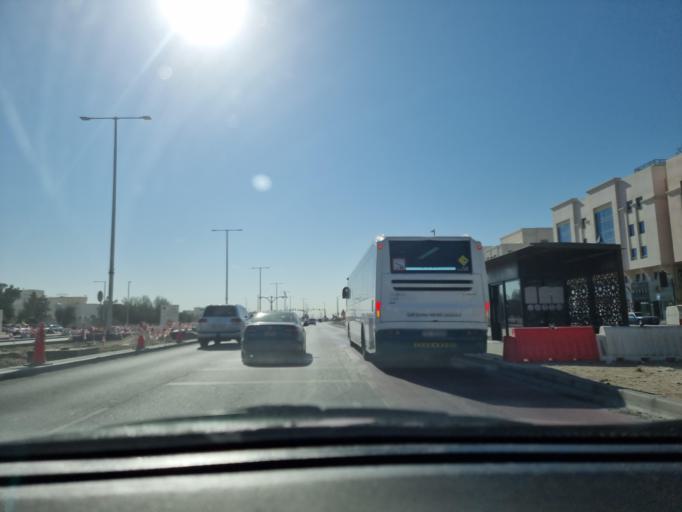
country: AE
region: Abu Dhabi
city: Abu Dhabi
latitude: 24.4213
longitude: 54.5657
